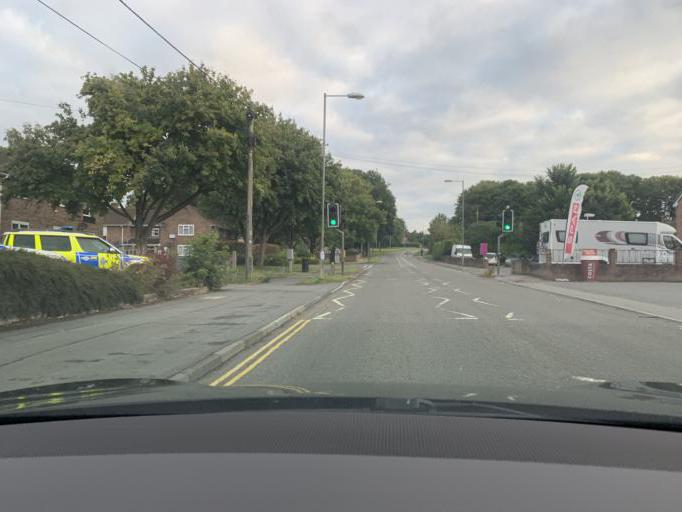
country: GB
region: England
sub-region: Wiltshire
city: Tidworth
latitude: 51.2426
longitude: -1.6648
